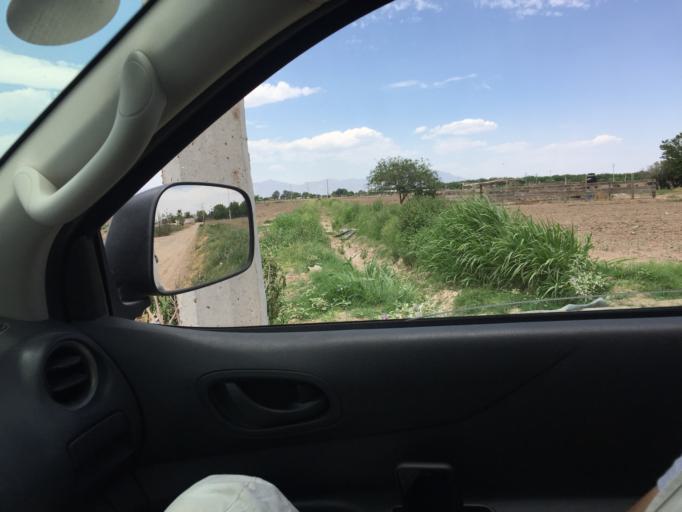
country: MX
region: Durango
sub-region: Gomez Palacio
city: San Jose de Vinedo
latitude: 25.6808
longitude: -103.4364
